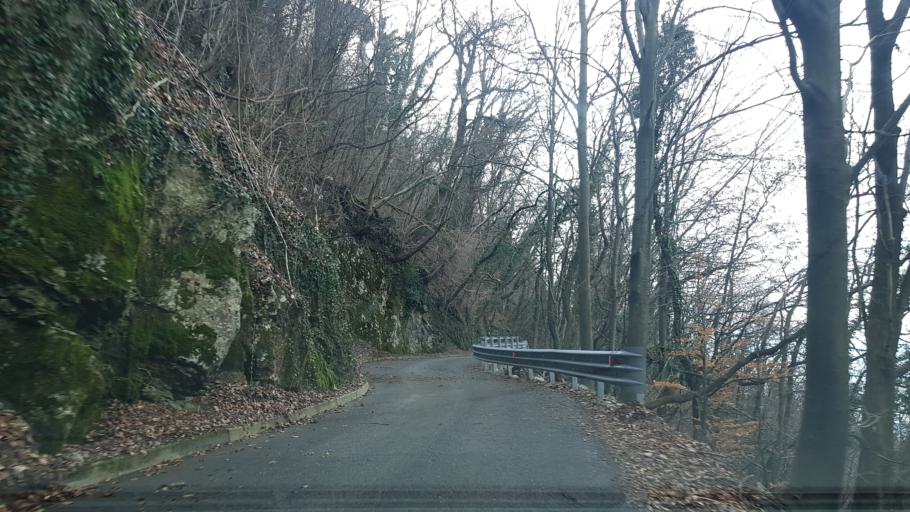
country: IT
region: Friuli Venezia Giulia
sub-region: Provincia di Udine
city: Clodig
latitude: 46.1765
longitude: 13.5780
